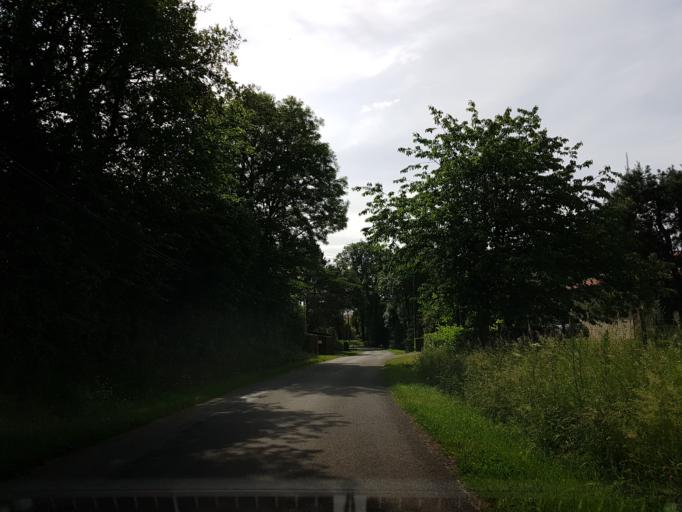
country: FR
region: Poitou-Charentes
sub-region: Departement de la Charente
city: Etagnac
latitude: 45.9334
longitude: 0.7355
